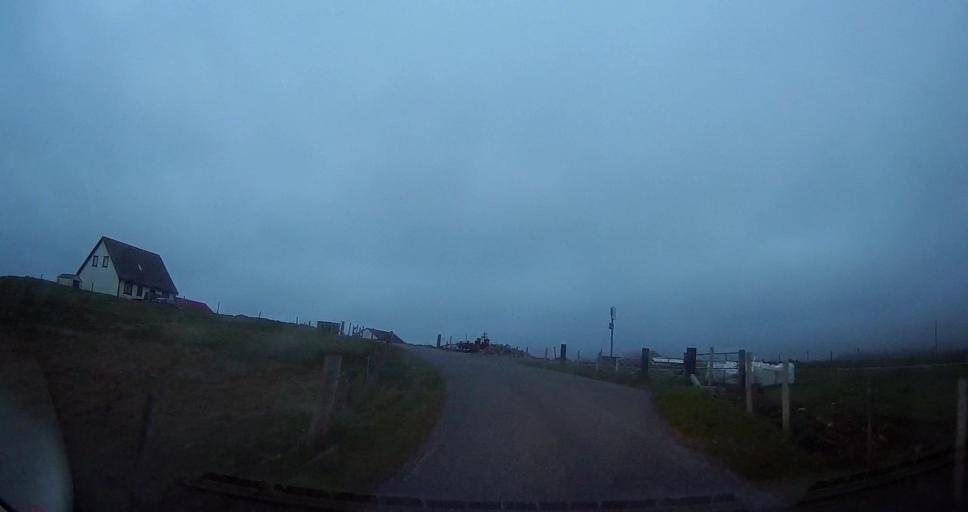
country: GB
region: Scotland
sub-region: Shetland Islands
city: Sandwick
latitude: 60.0410
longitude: -1.2186
